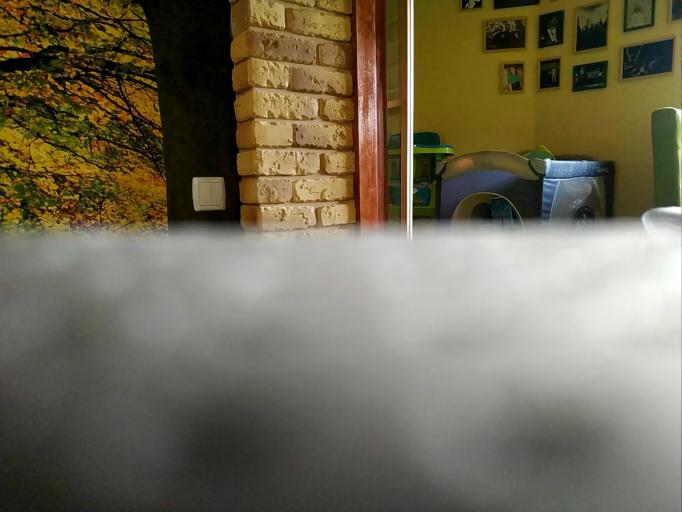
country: RU
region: Kaluga
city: Seredeyskiy
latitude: 54.0403
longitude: 35.3022
